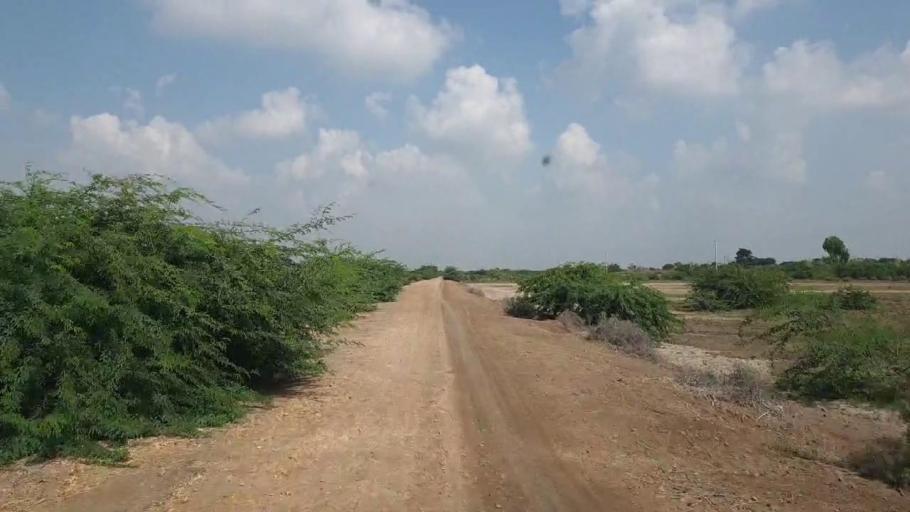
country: PK
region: Sindh
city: Badin
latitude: 24.4891
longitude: 68.6517
